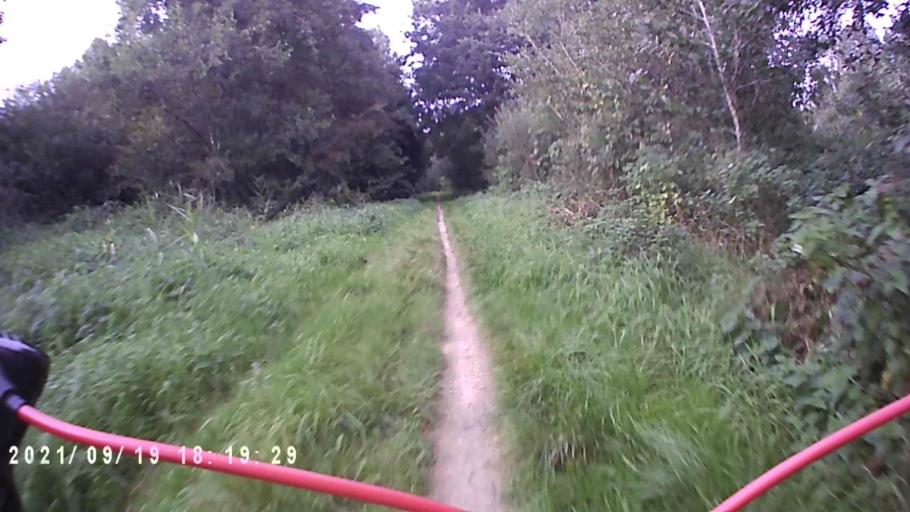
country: NL
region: Groningen
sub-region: Gemeente Appingedam
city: Appingedam
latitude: 53.2692
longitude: 6.8727
